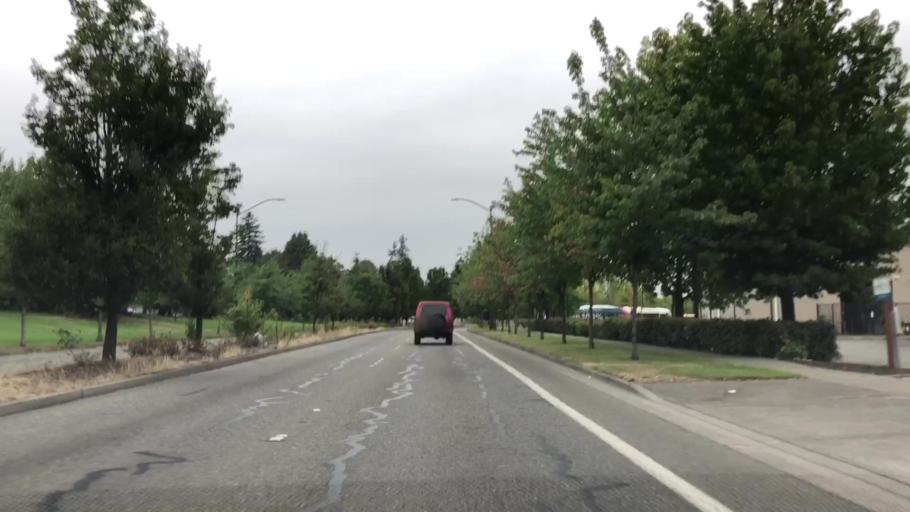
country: US
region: Washington
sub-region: Kitsap County
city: Navy Yard City
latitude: 47.5612
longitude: -122.6545
